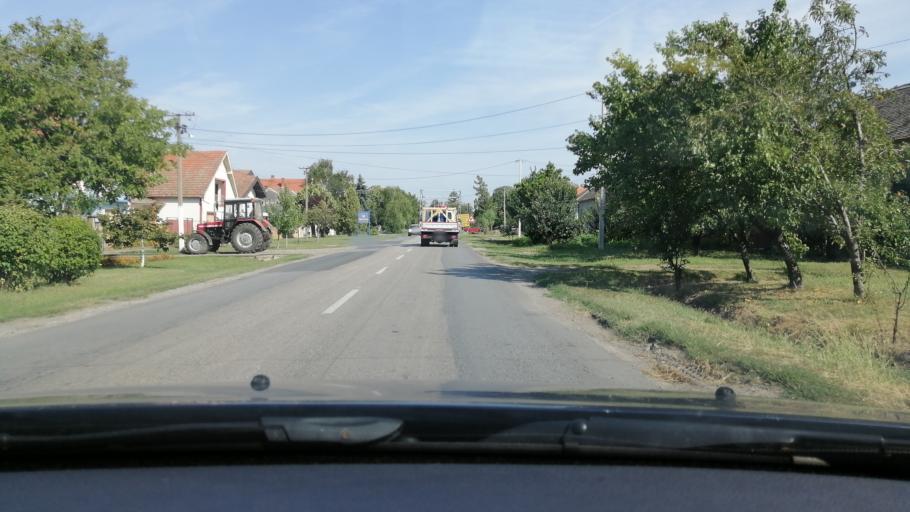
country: RS
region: Autonomna Pokrajina Vojvodina
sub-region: Juznobanatski Okrug
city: Kovacica
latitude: 45.1164
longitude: 20.6173
